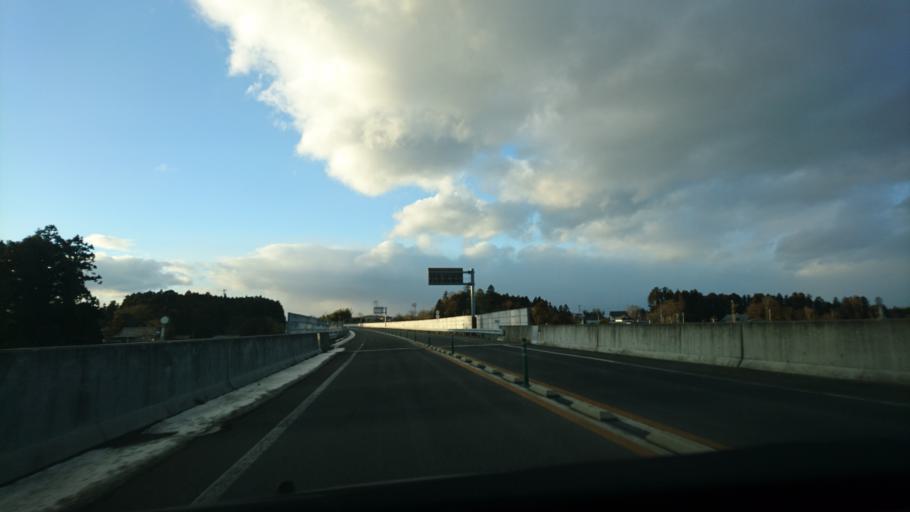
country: JP
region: Iwate
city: Ichinoseki
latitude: 38.7367
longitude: 141.1236
